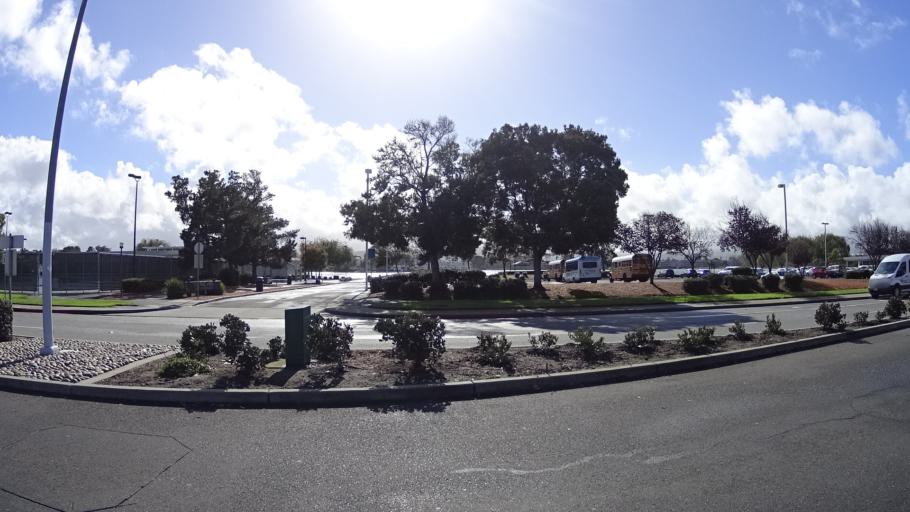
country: US
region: California
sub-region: San Mateo County
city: Foster City
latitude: 37.5570
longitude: -122.2682
